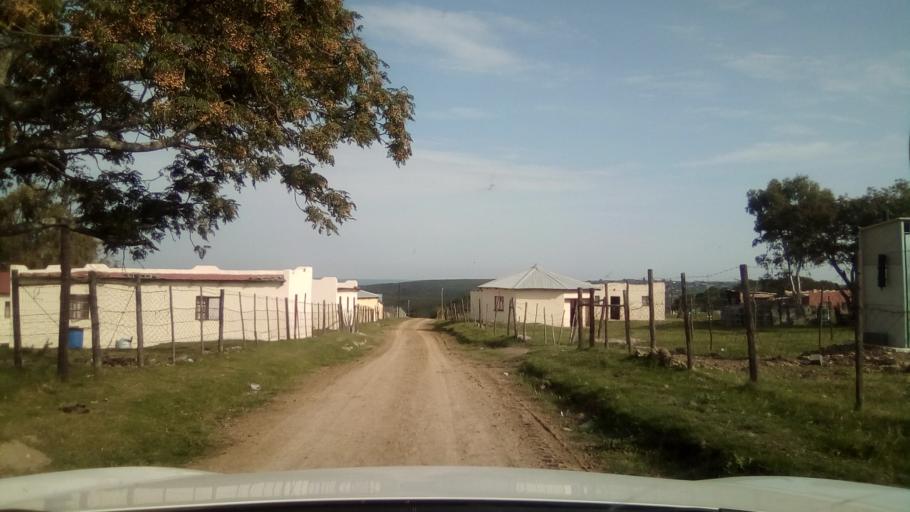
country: ZA
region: Eastern Cape
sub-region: Buffalo City Metropolitan Municipality
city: Bhisho
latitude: -33.0059
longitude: 27.3024
